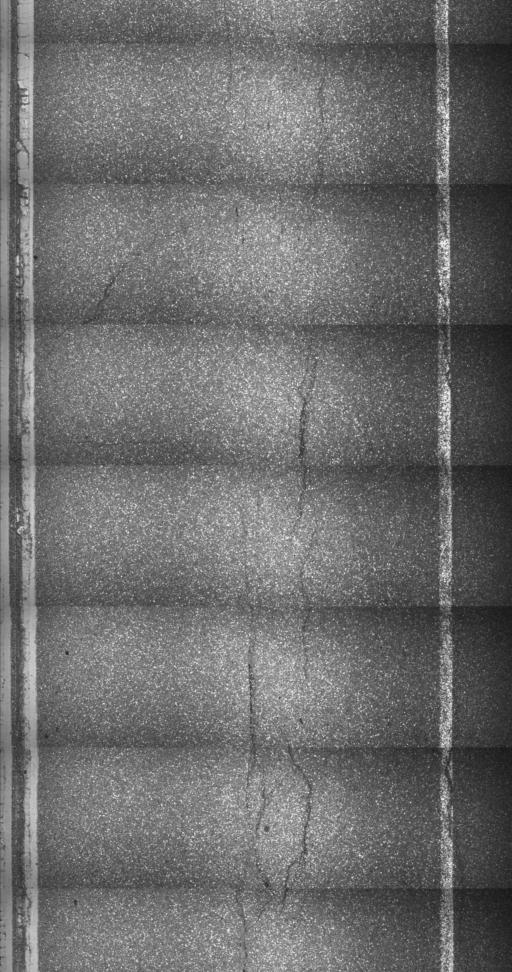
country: US
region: Vermont
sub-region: Windsor County
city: White River Junction
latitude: 43.6653
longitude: -72.3527
